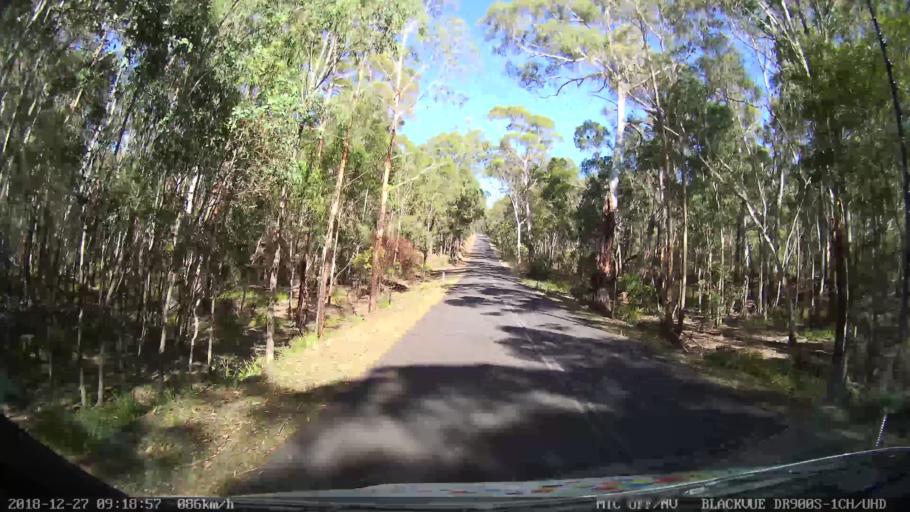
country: AU
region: New South Wales
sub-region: Lithgow
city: Portland
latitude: -33.1226
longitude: 150.0420
